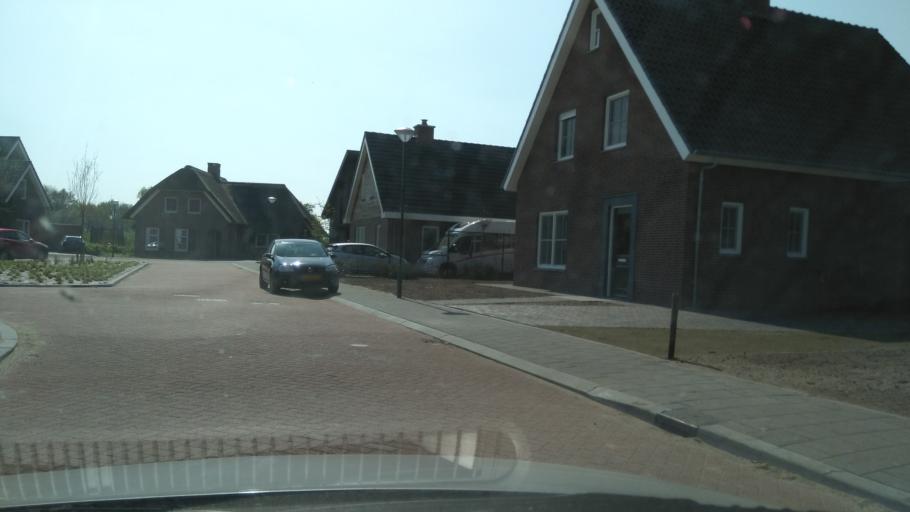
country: NL
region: North Brabant
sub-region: Gemeente Baarle-Nassau
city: Baarle-Nassau
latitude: 51.5005
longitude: 4.8670
